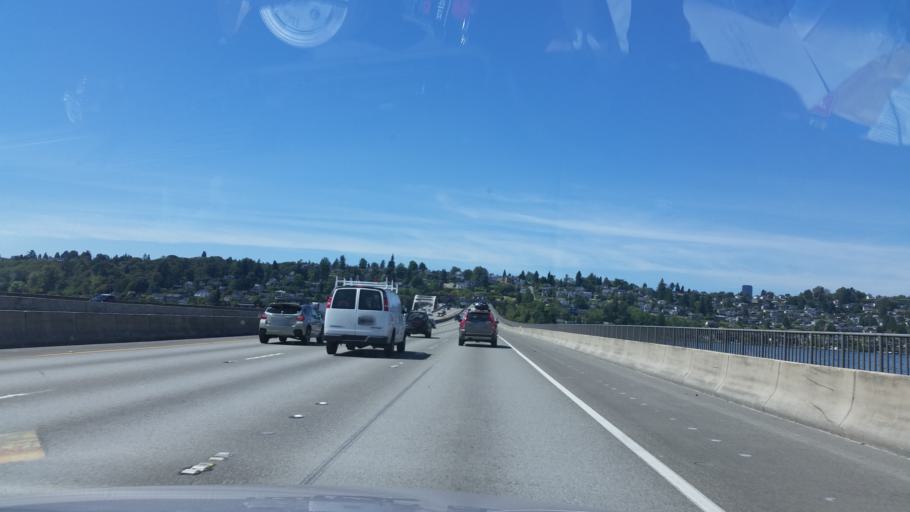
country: US
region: Washington
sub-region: King County
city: Mercer Island
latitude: 47.5901
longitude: -122.2746
